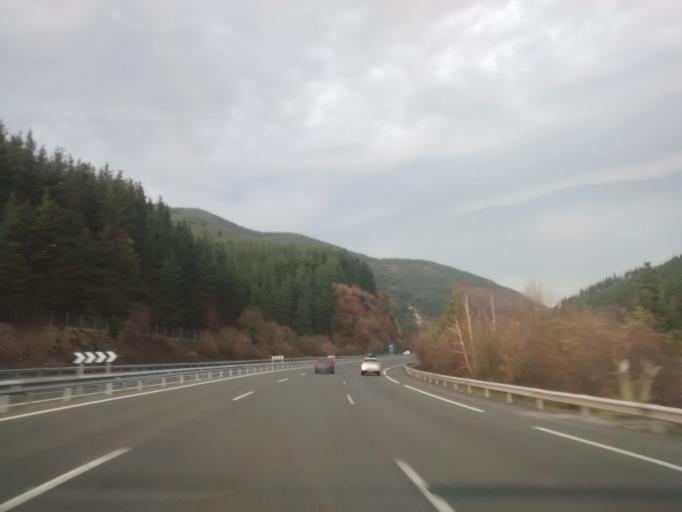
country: ES
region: Basque Country
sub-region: Provincia de Alava
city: Lezama
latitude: 43.0574
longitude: -2.9324
